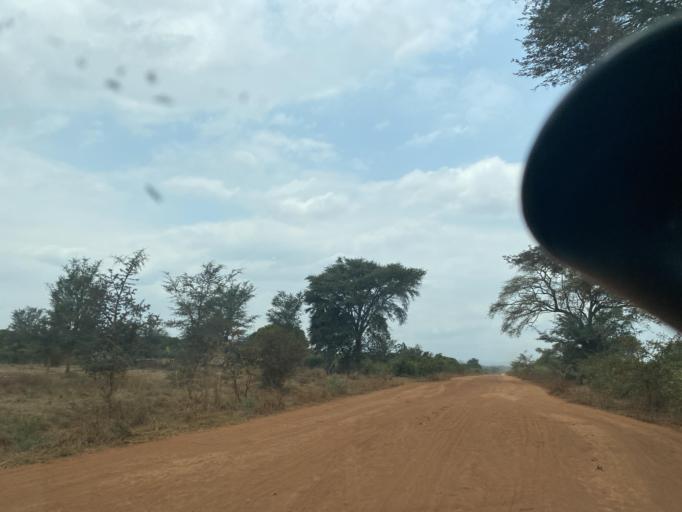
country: ZM
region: Lusaka
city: Chongwe
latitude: -15.5019
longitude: 28.8095
